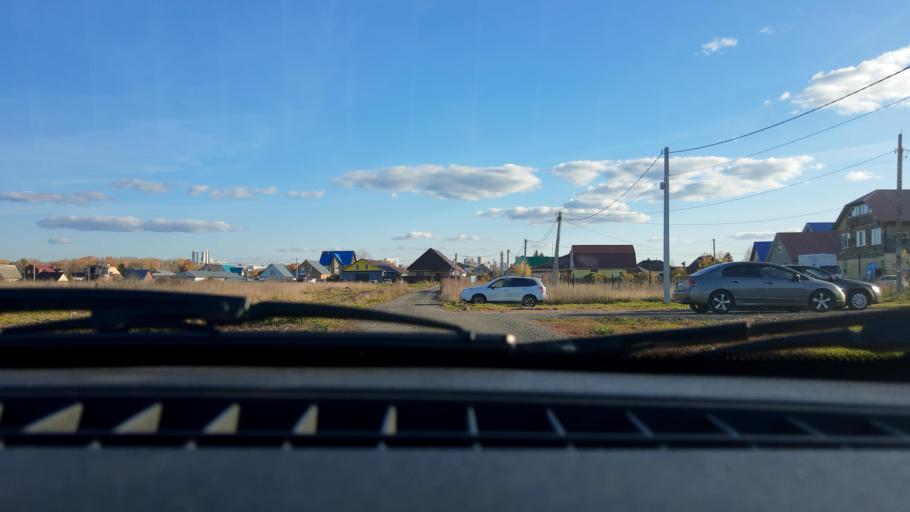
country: RU
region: Bashkortostan
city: Mikhaylovka
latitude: 54.7659
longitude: 55.9036
